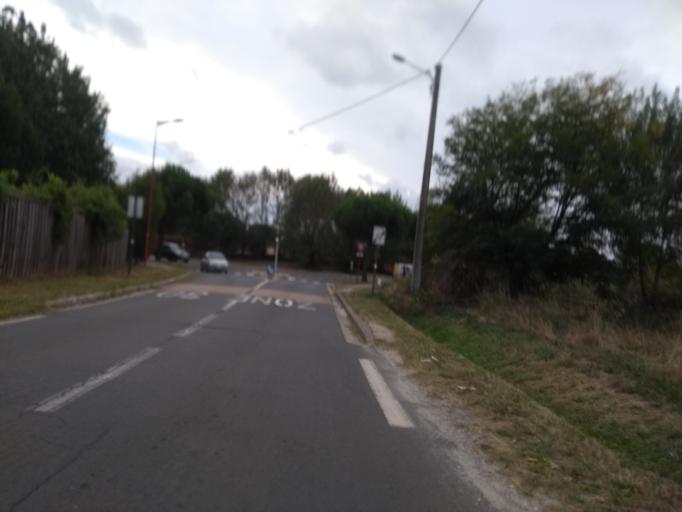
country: FR
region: Aquitaine
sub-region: Departement de la Gironde
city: Pessac
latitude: 44.8197
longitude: -0.6590
